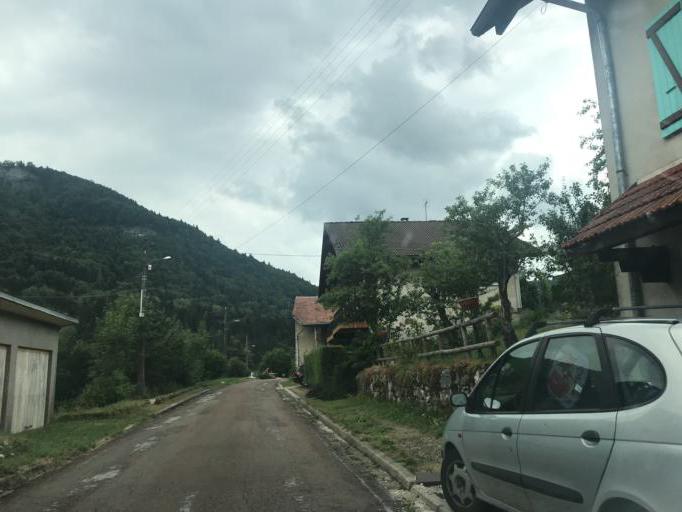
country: FR
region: Franche-Comte
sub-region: Departement du Jura
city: Saint-Claude
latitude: 46.3438
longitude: 5.8358
